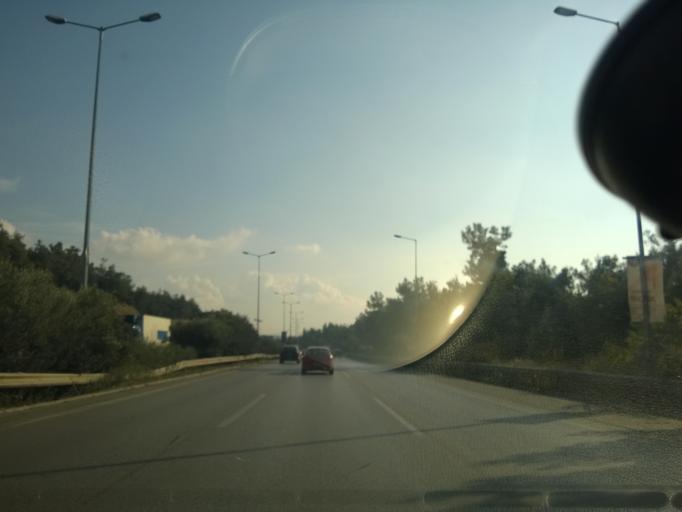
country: GR
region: Central Macedonia
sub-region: Nomos Thessalonikis
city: Triandria
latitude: 40.6201
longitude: 22.9827
